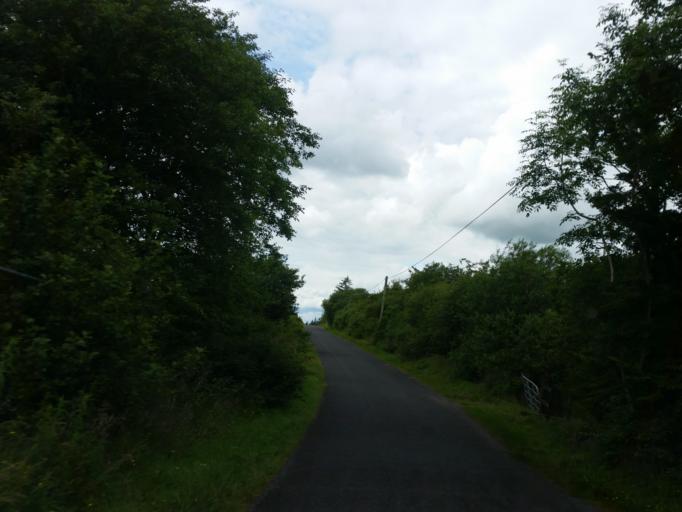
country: IE
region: Ulster
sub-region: County Monaghan
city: Clones
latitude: 54.2756
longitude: -7.2746
